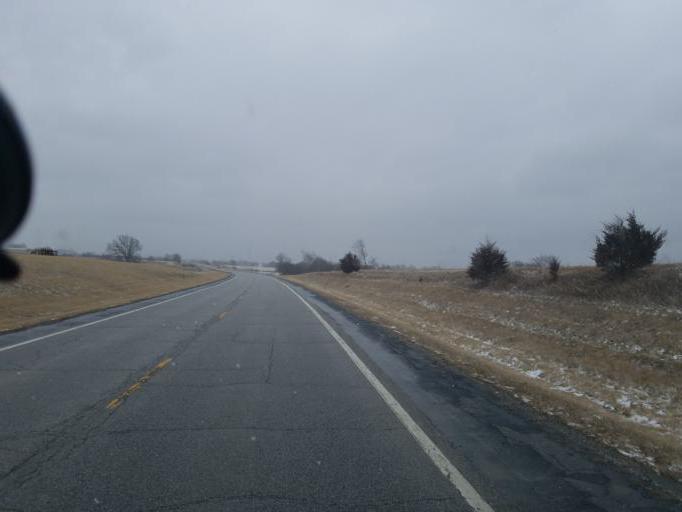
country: US
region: Missouri
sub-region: Putnam County
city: Unionville
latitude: 40.4655
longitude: -92.8358
